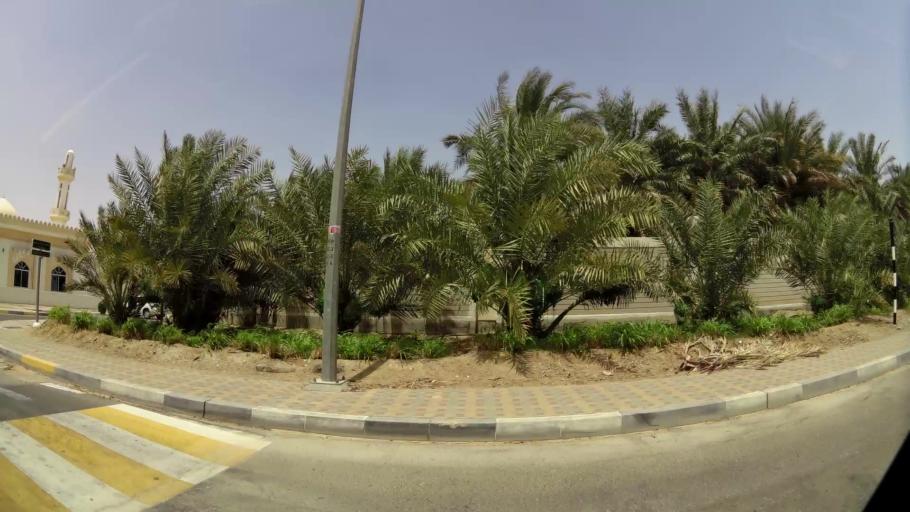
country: AE
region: Abu Dhabi
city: Al Ain
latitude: 24.1991
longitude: 55.7092
